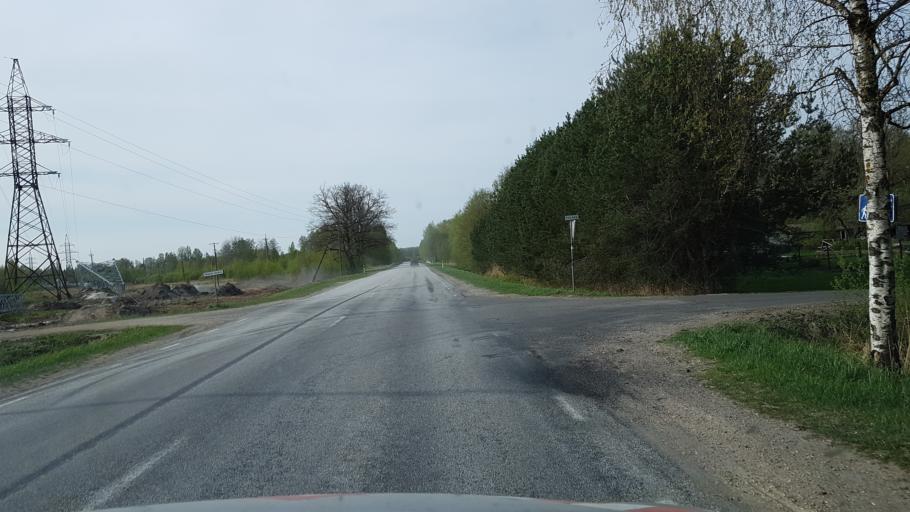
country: EE
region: Paernumaa
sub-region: Audru vald
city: Audru
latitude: 58.4125
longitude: 24.3096
